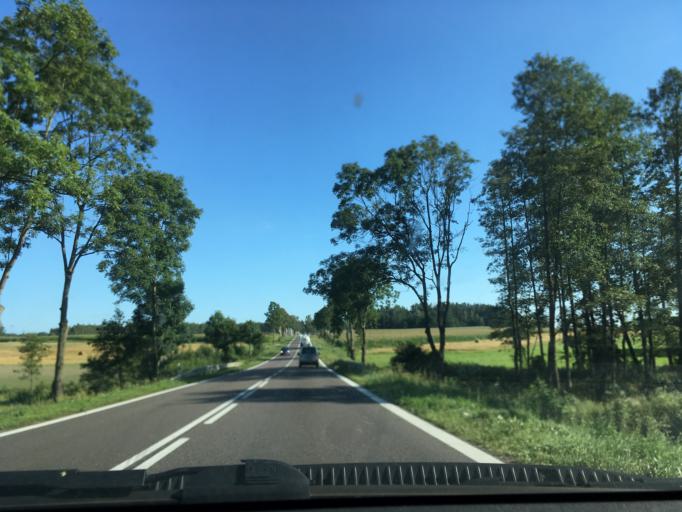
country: PL
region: Podlasie
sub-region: Powiat sokolski
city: Janow
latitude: 53.4164
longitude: 23.1148
